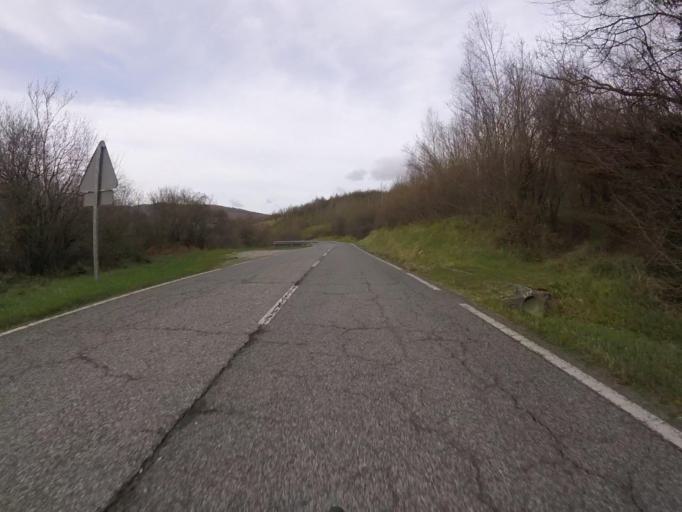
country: ES
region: Navarre
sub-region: Provincia de Navarra
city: Olazagutia
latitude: 42.8655
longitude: -2.1849
